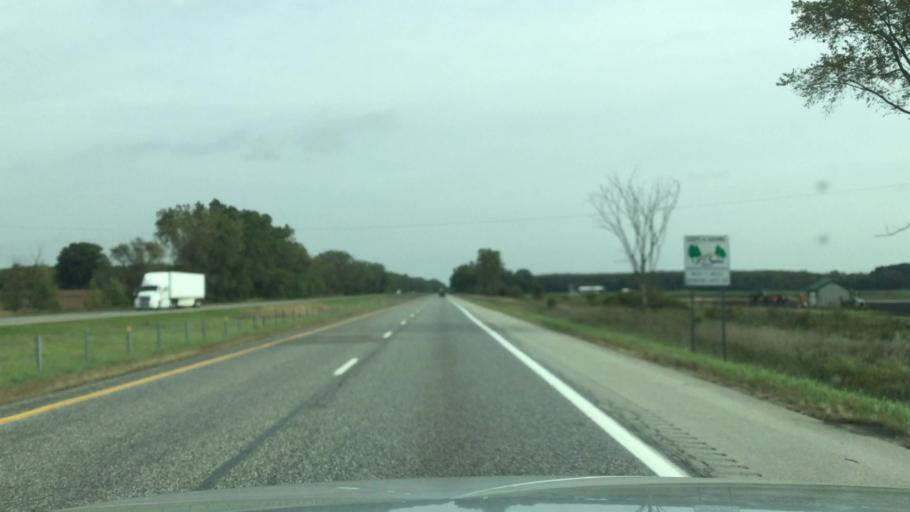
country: US
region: Michigan
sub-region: Shiawassee County
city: Corunna
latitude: 42.8788
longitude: -84.1223
